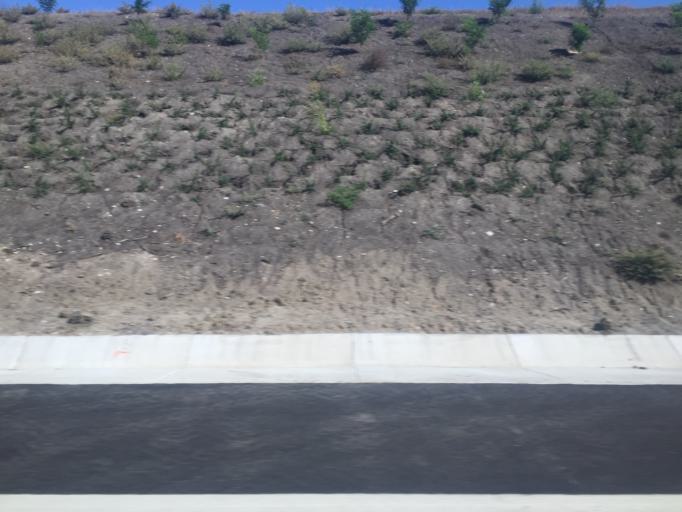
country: TR
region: Bursa
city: Mahmudiye
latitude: 40.2570
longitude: 28.7157
